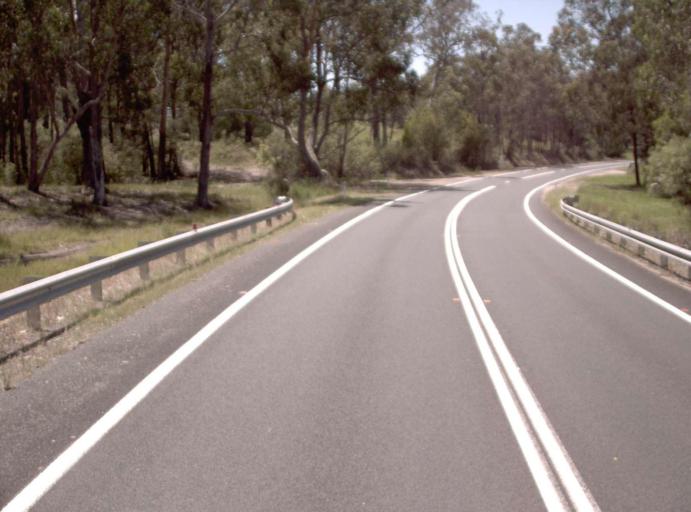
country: AU
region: Victoria
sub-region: East Gippsland
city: Lakes Entrance
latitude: -37.7349
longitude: 148.0832
